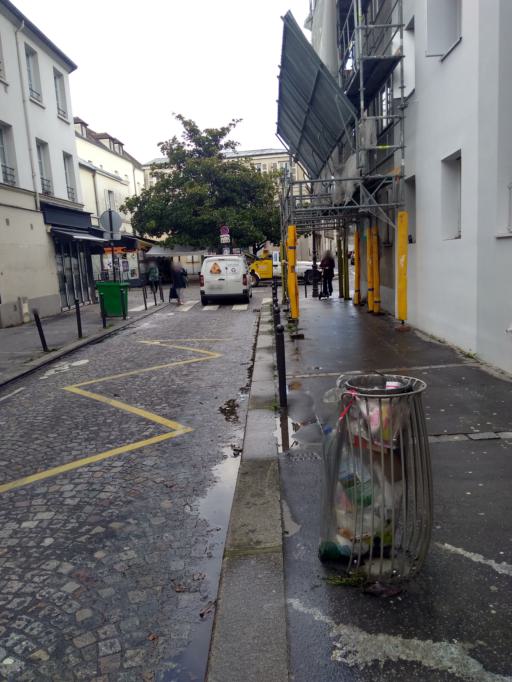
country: FR
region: Ile-de-France
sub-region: Departement de Seine-Saint-Denis
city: Bagnolet
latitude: 48.8587
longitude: 2.4056
